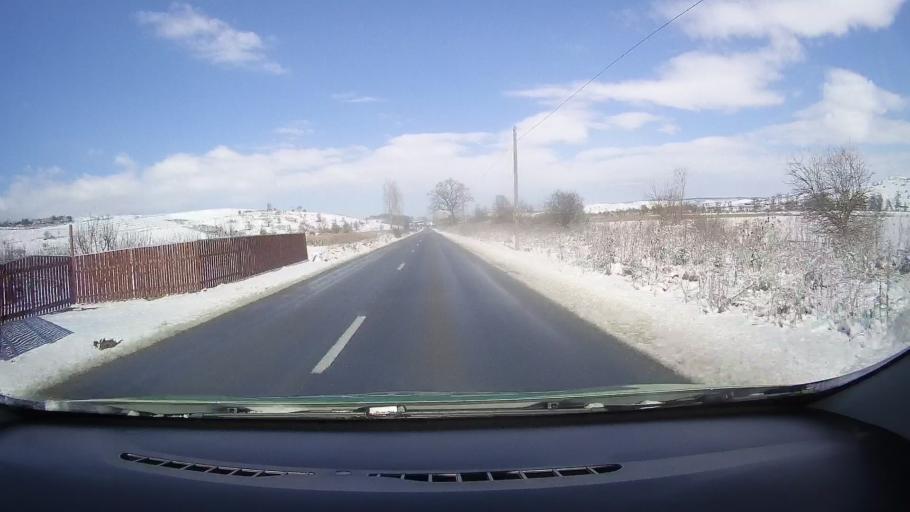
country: RO
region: Sibiu
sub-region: Comuna Nocrich
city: Nocrich
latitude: 45.8775
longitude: 24.4516
